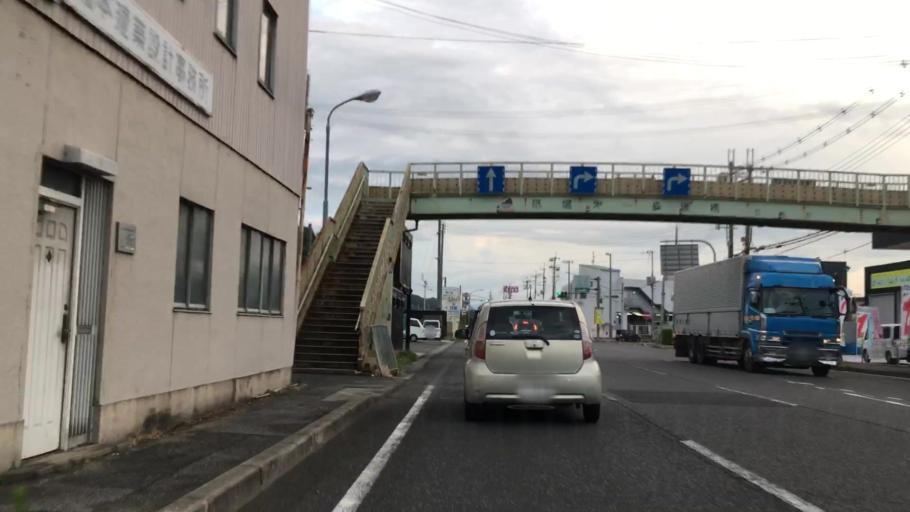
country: JP
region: Hyogo
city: Himeji
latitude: 34.8716
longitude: 134.7293
